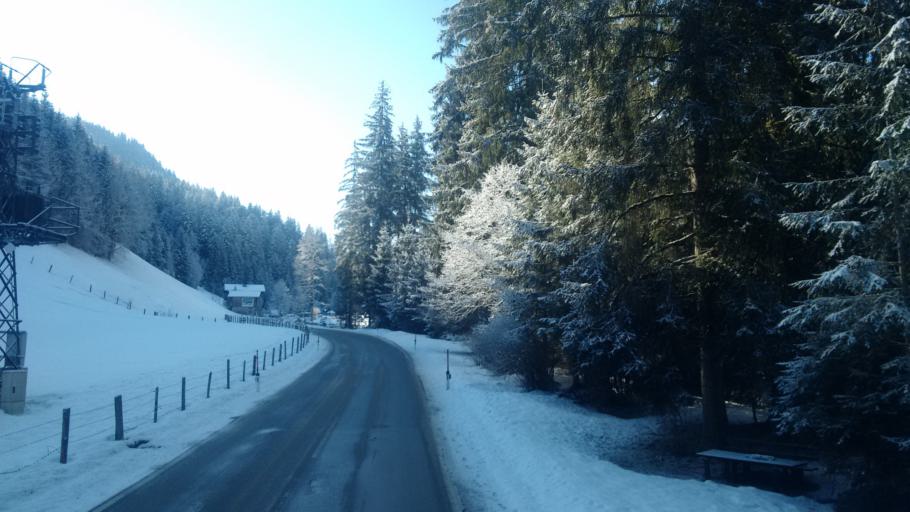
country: AT
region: Salzburg
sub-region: Politischer Bezirk Sankt Johann im Pongau
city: Altenmarkt im Pongau
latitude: 47.3555
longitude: 13.4275
